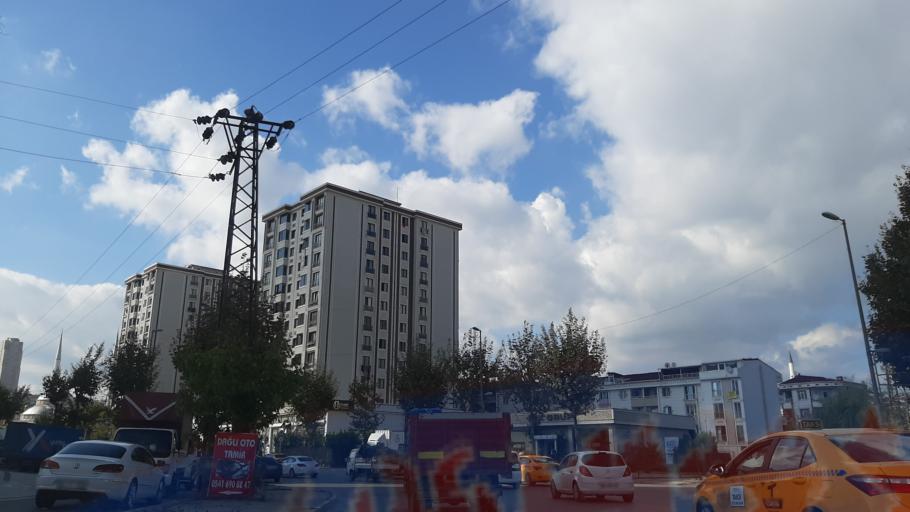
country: TR
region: Istanbul
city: Esenyurt
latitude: 41.0299
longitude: 28.6655
